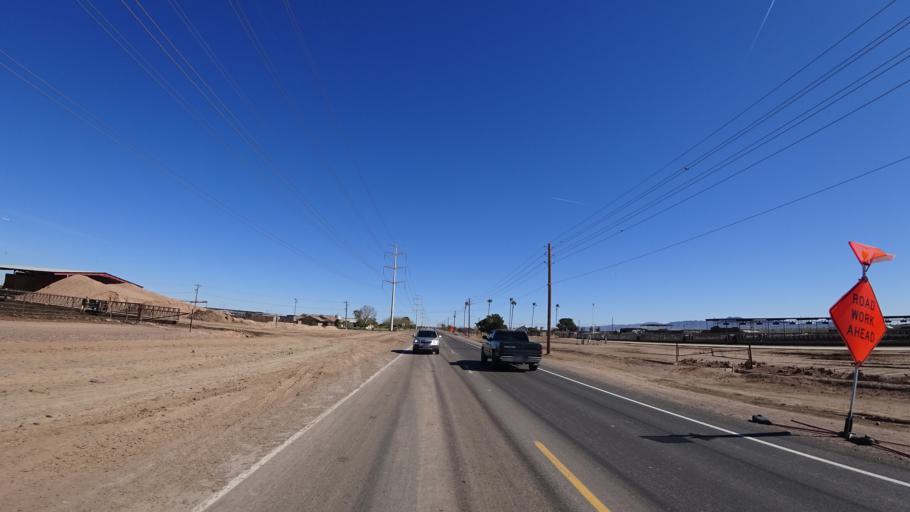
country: US
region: Arizona
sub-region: Maricopa County
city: Tolleson
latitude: 33.4073
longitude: -112.2477
